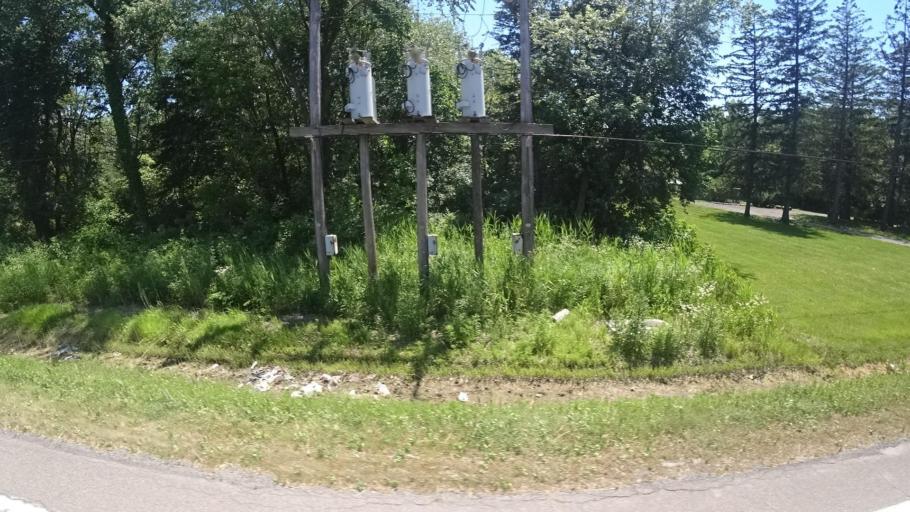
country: US
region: Indiana
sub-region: Porter County
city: Burns Harbor
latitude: 41.6001
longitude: -87.1366
